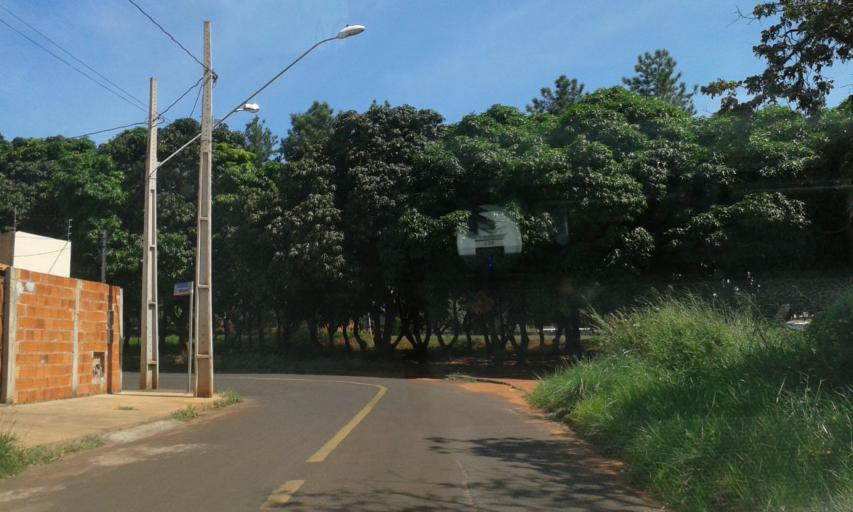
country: BR
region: Minas Gerais
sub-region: Santa Vitoria
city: Santa Vitoria
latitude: -18.8558
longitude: -50.1292
